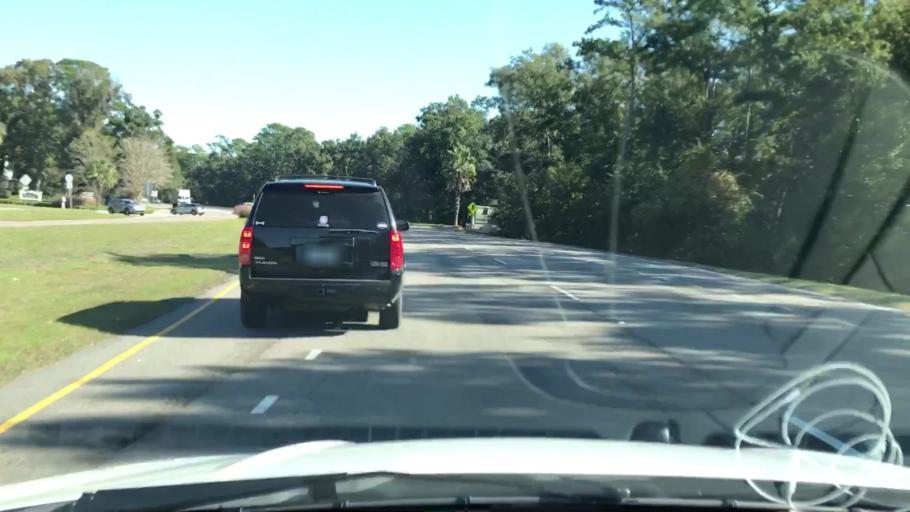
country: US
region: South Carolina
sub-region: Beaufort County
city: Hilton Head Island
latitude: 32.2124
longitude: -80.7269
